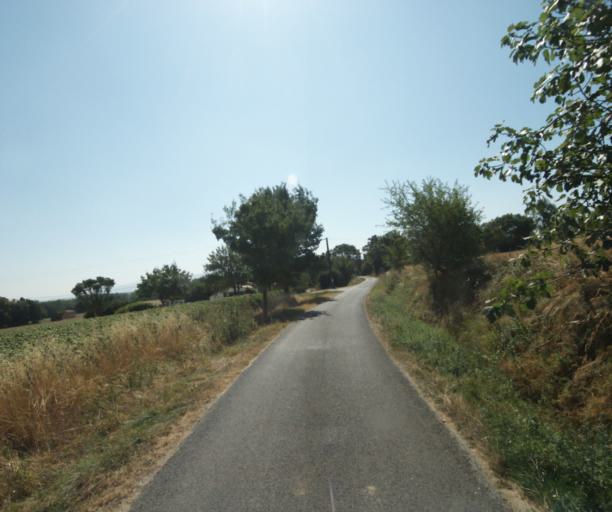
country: FR
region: Midi-Pyrenees
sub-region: Departement de la Haute-Garonne
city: Saint-Felix-Lauragais
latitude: 43.5059
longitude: 1.9397
